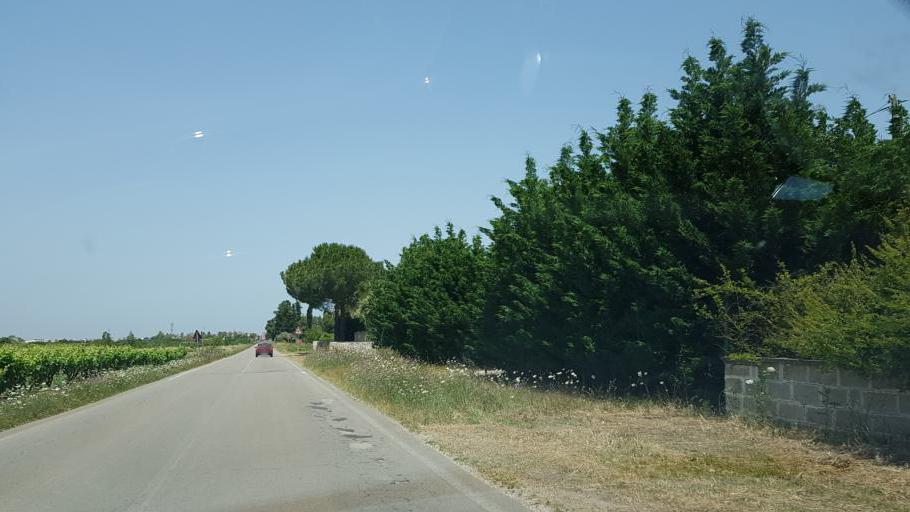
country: IT
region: Apulia
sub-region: Provincia di Brindisi
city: San Pancrazio Salentino
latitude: 40.4012
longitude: 17.8354
